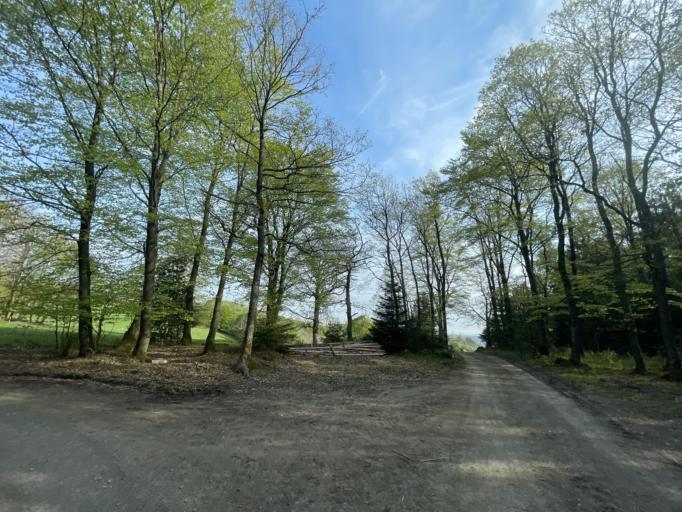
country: DE
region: North Rhine-Westphalia
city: Werdohl
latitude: 51.2155
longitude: 7.8101
